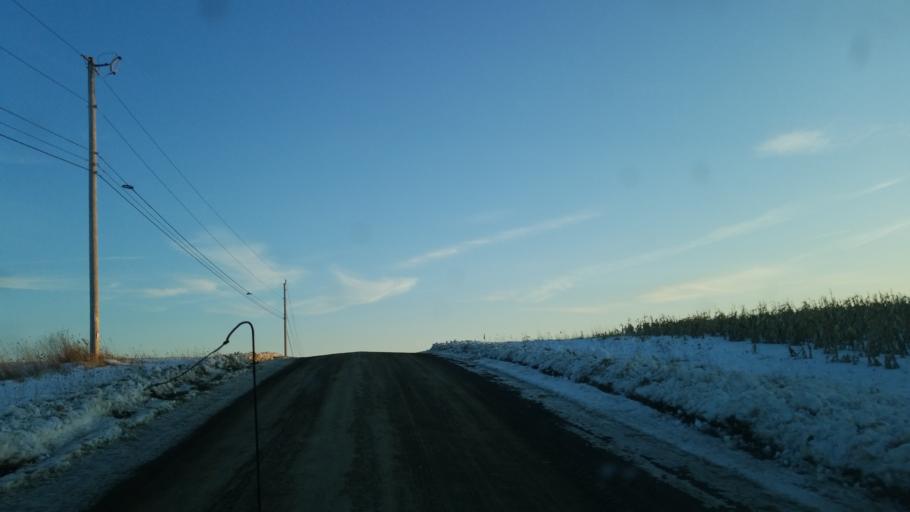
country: US
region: Pennsylvania
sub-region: Tioga County
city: Westfield
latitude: 42.0266
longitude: -77.6197
